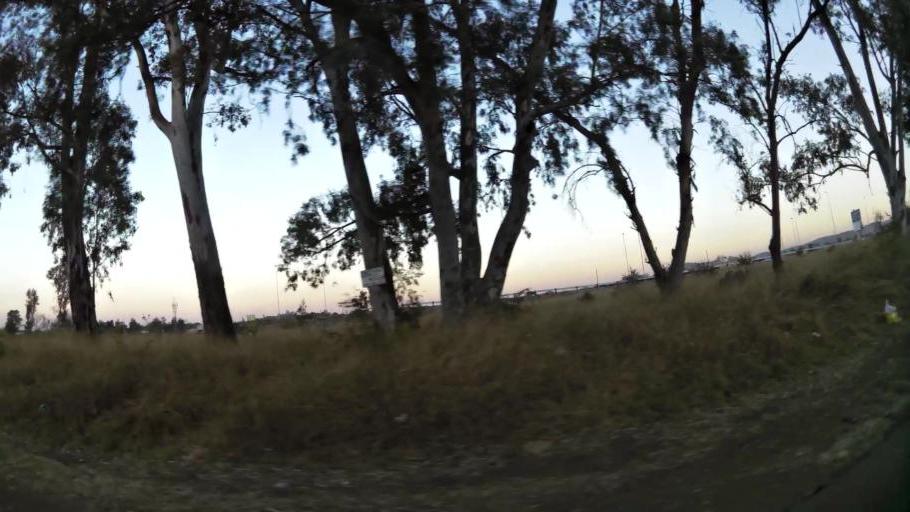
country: ZA
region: North-West
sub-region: Bojanala Platinum District Municipality
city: Rustenburg
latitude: -25.6599
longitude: 27.2353
